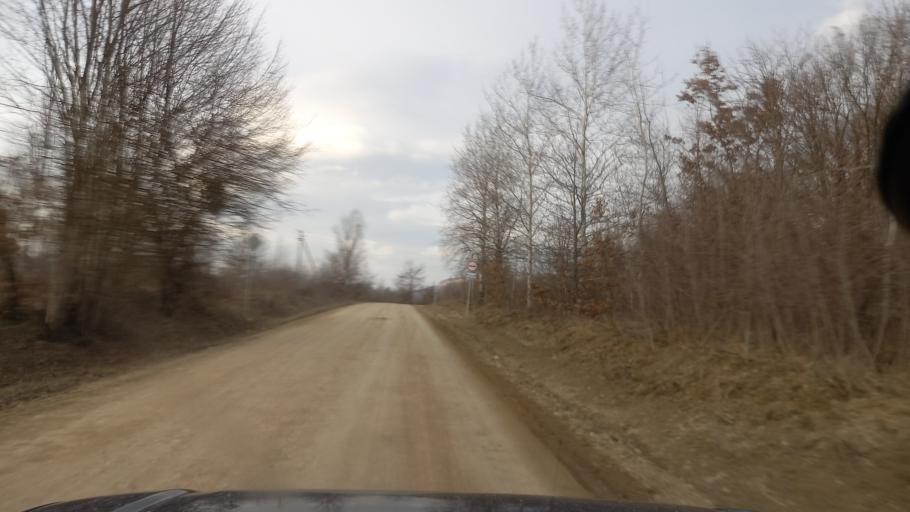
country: RU
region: Adygeya
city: Kamennomostskiy
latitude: 44.1685
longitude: 40.2465
